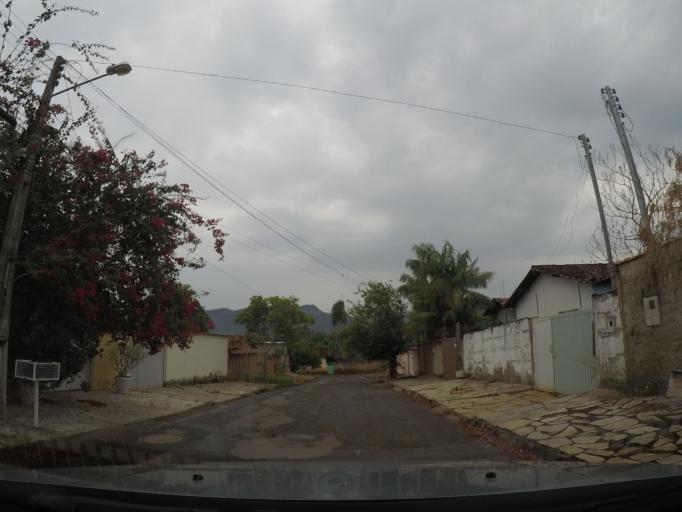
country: BR
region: Goias
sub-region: Pirenopolis
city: Pirenopolis
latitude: -15.8499
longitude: -48.9497
